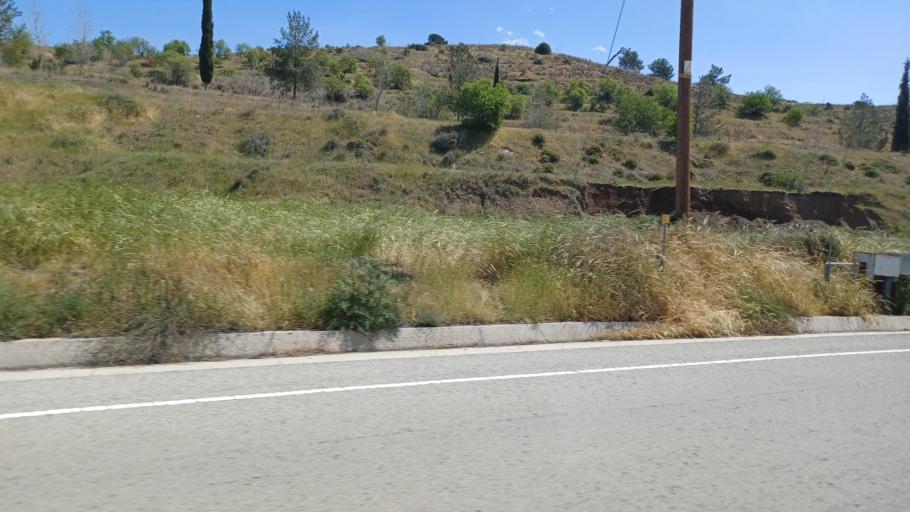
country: CY
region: Lefkosia
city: Astromeritis
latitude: 35.0588
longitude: 33.0276
